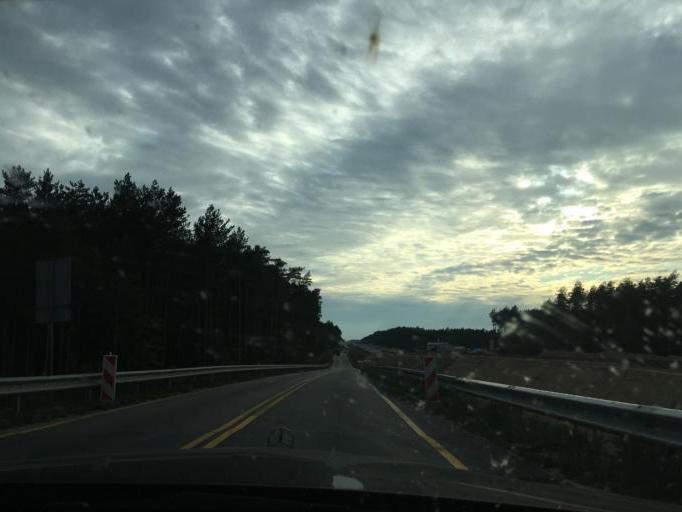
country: PL
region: Masovian Voivodeship
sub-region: Powiat ostrowski
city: Ostrow Mazowiecka
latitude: 52.7778
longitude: 21.8447
